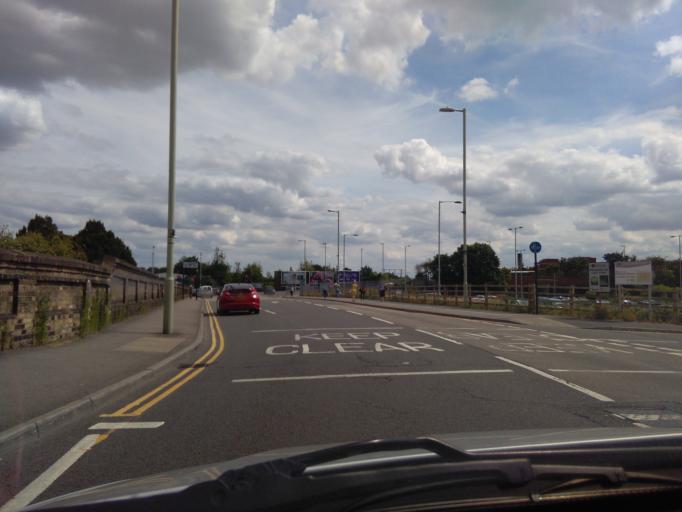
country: GB
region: England
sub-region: Bedford
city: Bedford
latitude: 52.1320
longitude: -0.4718
